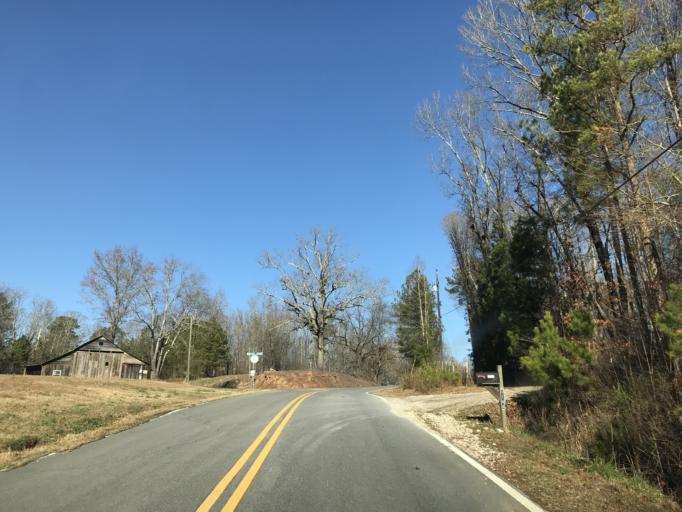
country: US
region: Georgia
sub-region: Paulding County
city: Dallas
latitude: 34.0011
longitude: -84.8976
